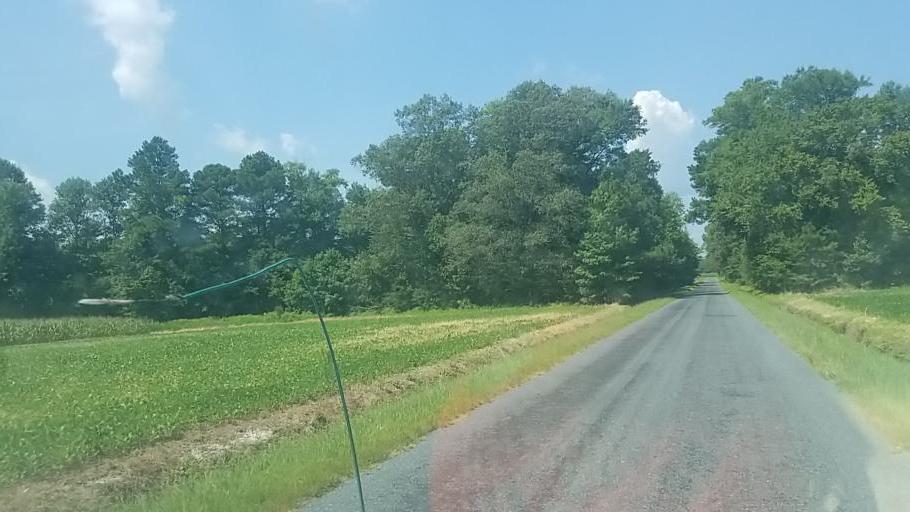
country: US
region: Maryland
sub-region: Worcester County
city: Berlin
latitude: 38.2976
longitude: -75.2855
